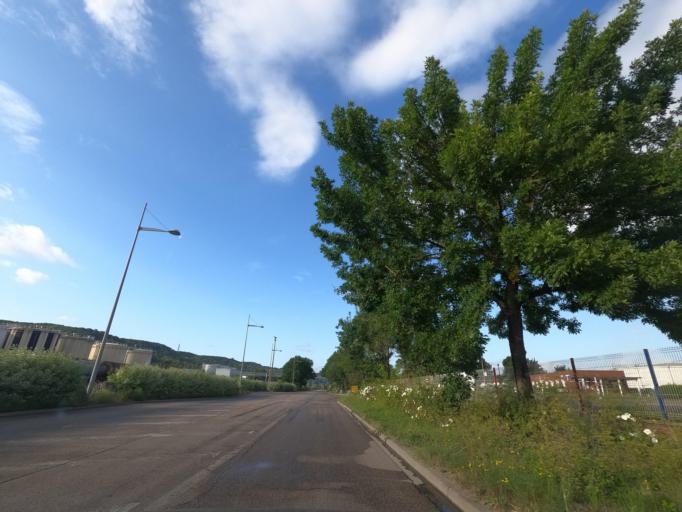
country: FR
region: Haute-Normandie
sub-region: Departement de la Seine-Maritime
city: Petit-Couronne
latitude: 49.4086
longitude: 1.0171
